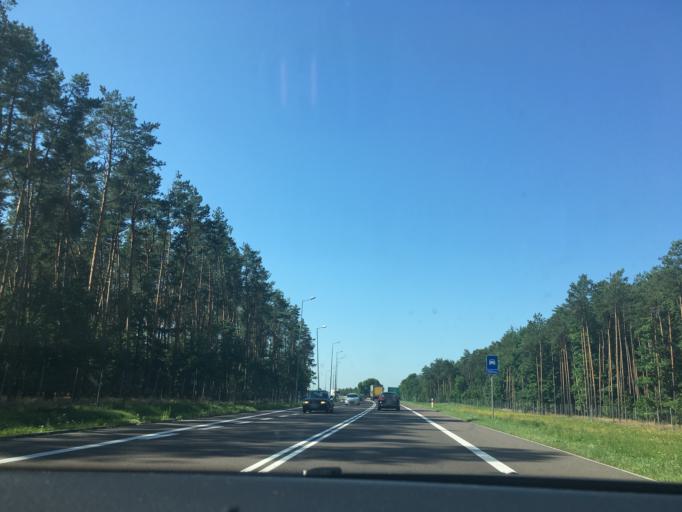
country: PL
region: Lublin Voivodeship
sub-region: Powiat lubartowski
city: Kock
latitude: 51.6640
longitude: 22.4684
